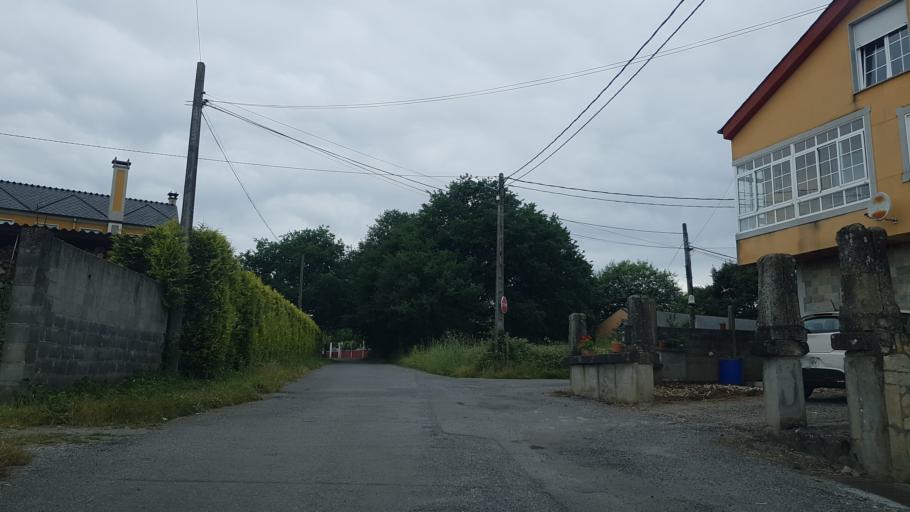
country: ES
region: Galicia
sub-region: Provincia de Lugo
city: Lugo
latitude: 43.0319
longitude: -7.5471
